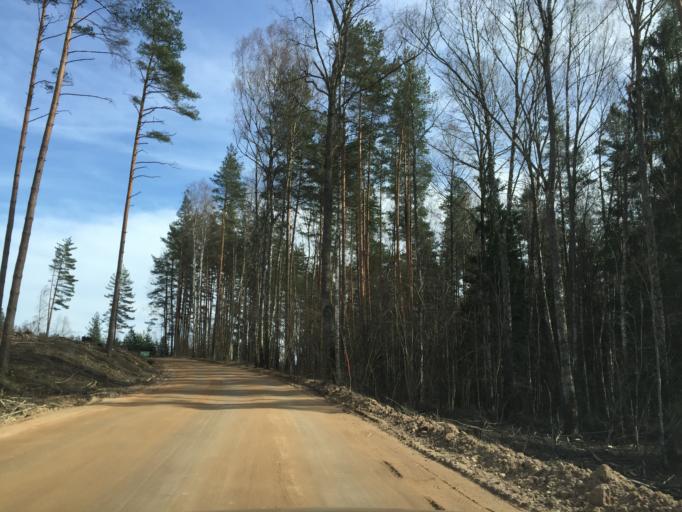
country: LV
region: Ikskile
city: Ikskile
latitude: 56.8434
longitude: 24.5414
